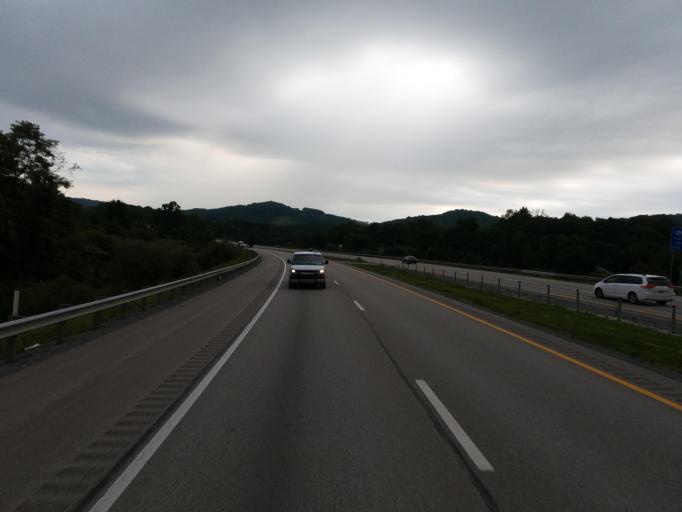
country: US
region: West Virginia
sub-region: Monongalia County
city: Morgantown
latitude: 39.5422
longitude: -79.9861
